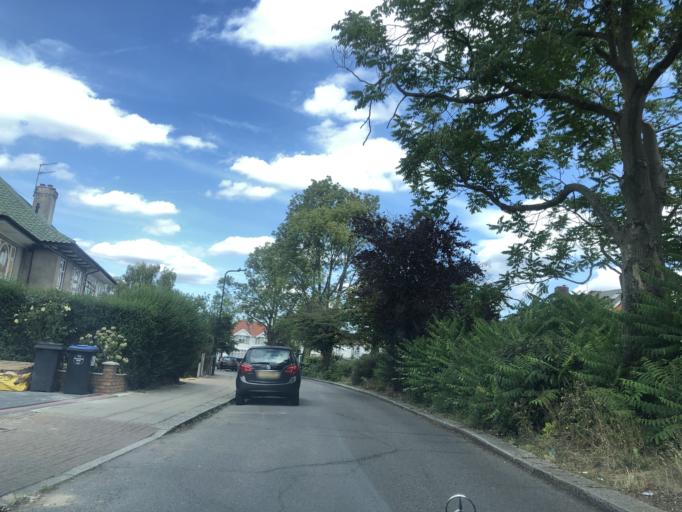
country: GB
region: England
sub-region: Greater London
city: Edgware
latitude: 51.5849
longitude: -0.2880
